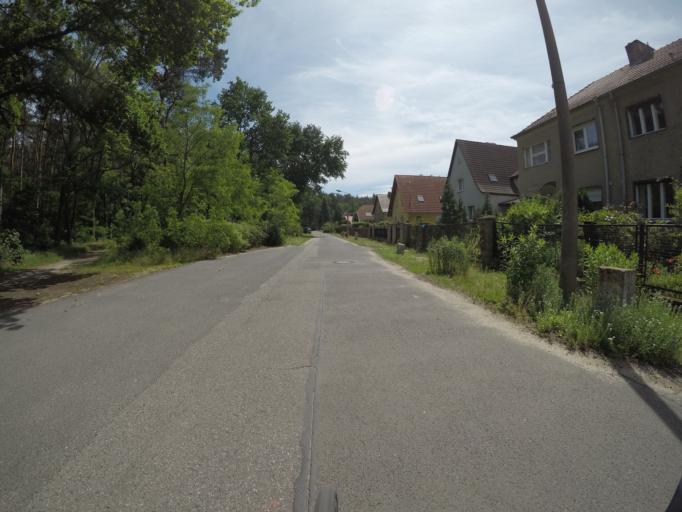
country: DE
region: Berlin
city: Berlin Koepenick
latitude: 52.4662
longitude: 13.5951
